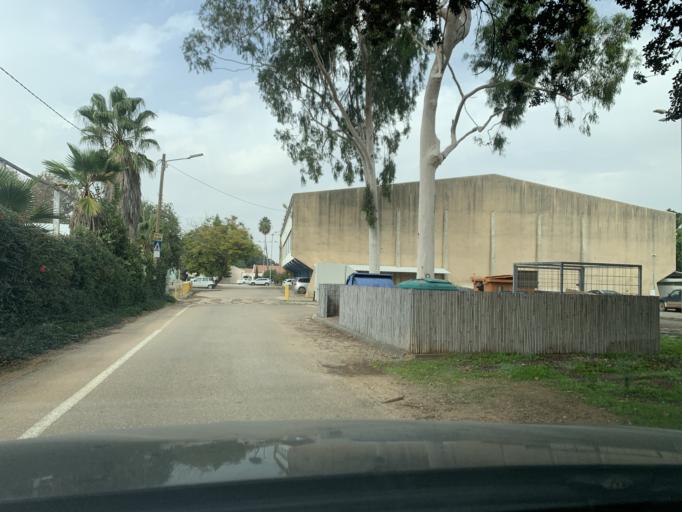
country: IL
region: Central District
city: Tirah
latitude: 32.2155
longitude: 34.9380
